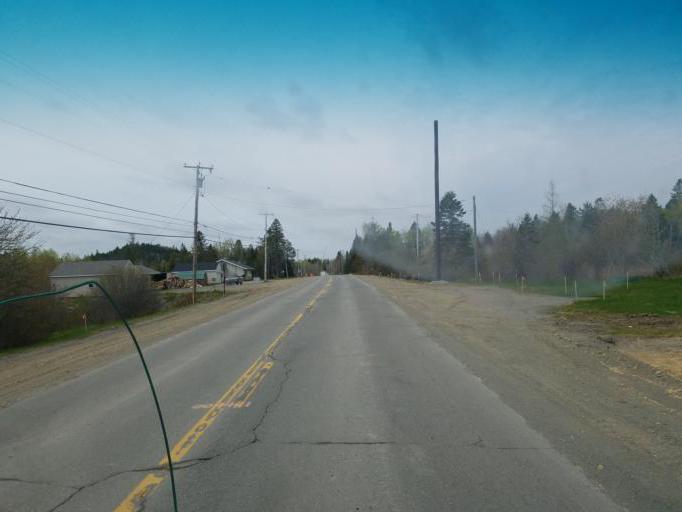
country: US
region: Maine
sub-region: Washington County
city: East Machias
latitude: 44.7877
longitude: -67.1842
